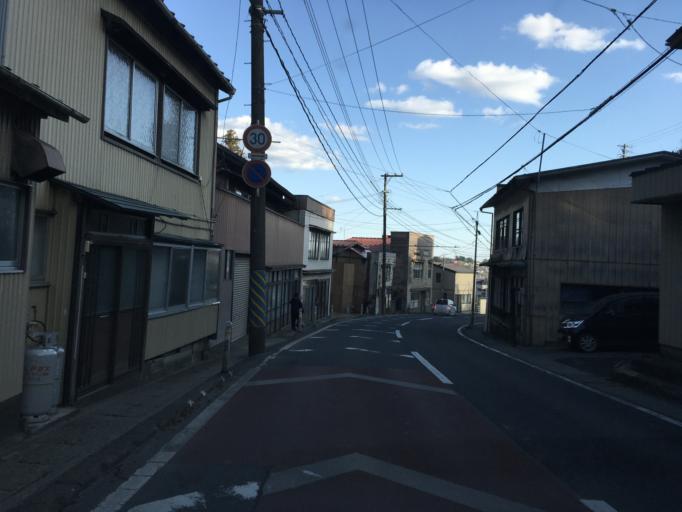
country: JP
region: Iwate
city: Ofunato
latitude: 38.9028
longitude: 141.5646
